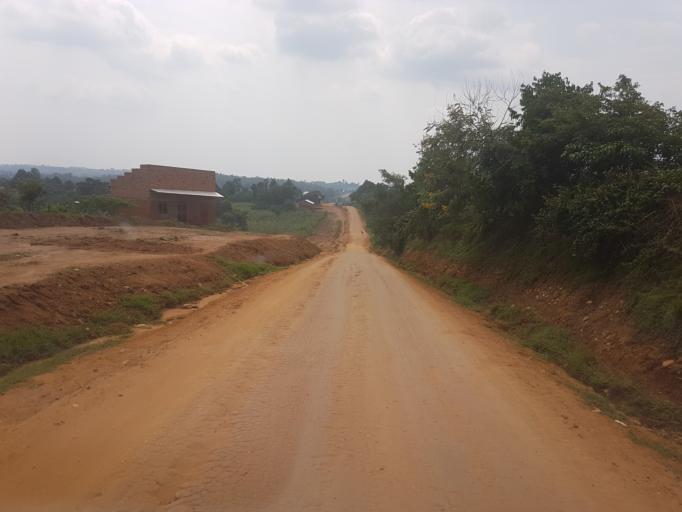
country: UG
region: Western Region
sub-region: Kanungu District
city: Ntungamo
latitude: -0.8087
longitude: 29.7054
